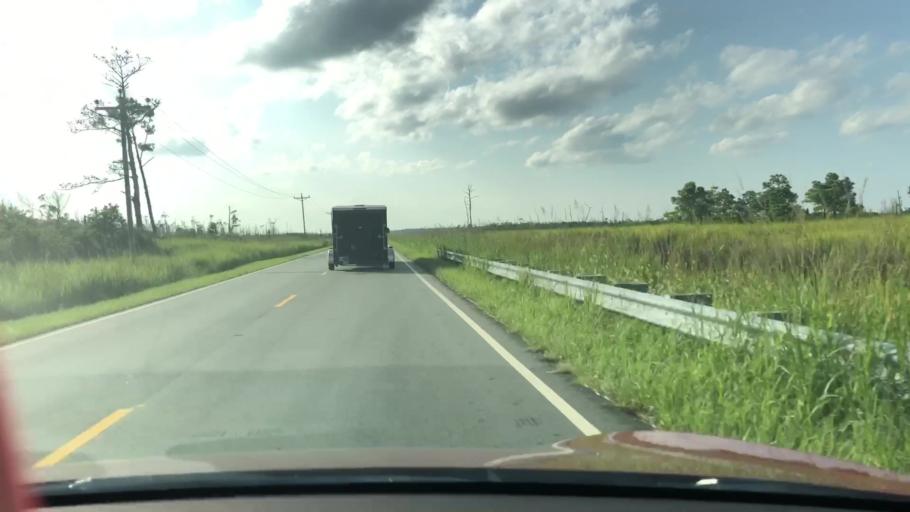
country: US
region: North Carolina
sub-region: Dare County
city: Wanchese
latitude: 35.6230
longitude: -75.8423
